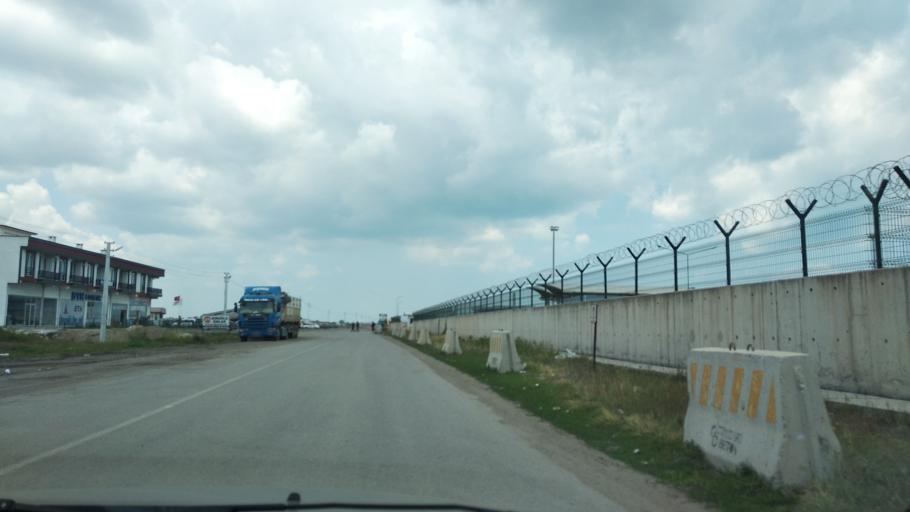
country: TR
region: Sakarya
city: Karasu
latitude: 41.1181
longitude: 30.6714
